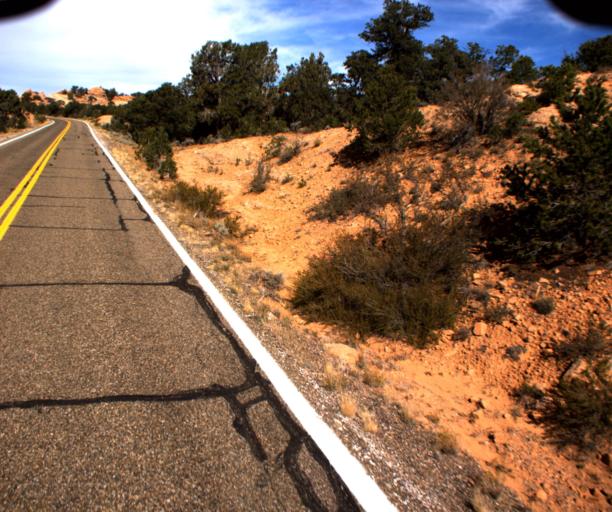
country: US
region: Arizona
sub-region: Navajo County
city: Kayenta
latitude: 36.6666
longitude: -110.5292
